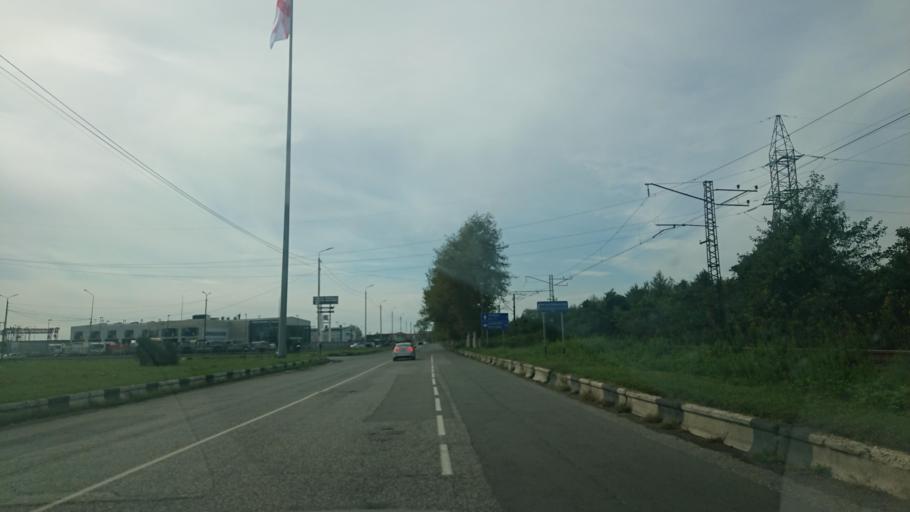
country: GE
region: Samegrelo and Zemo Svaneti
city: P'ot'i
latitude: 42.1725
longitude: 41.6777
